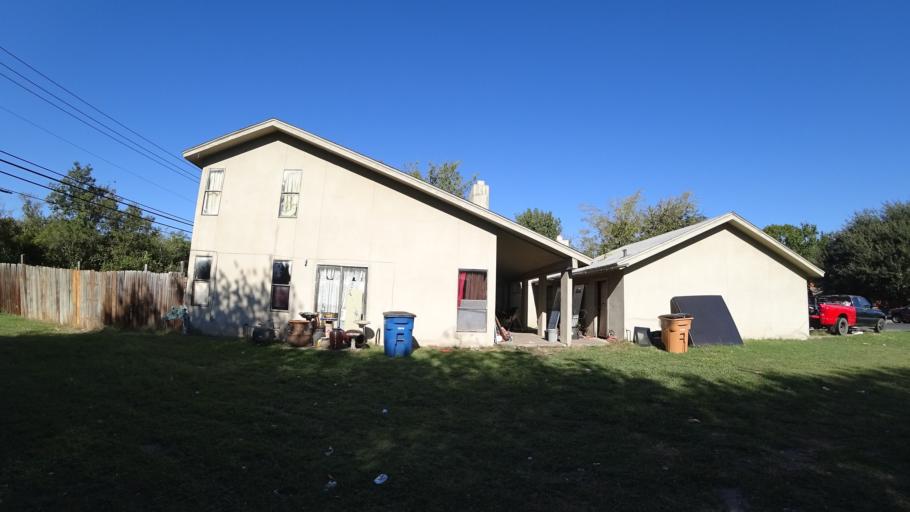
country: US
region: Texas
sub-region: Travis County
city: Austin
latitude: 30.3106
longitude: -97.6580
